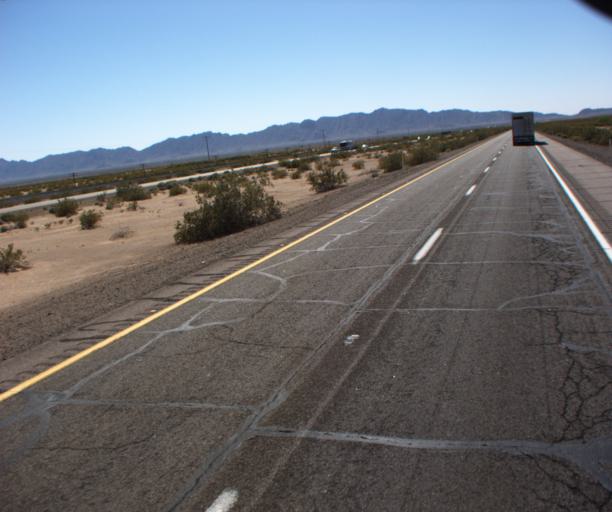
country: US
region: Arizona
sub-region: Yuma County
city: Wellton
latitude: 32.7652
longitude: -113.6244
